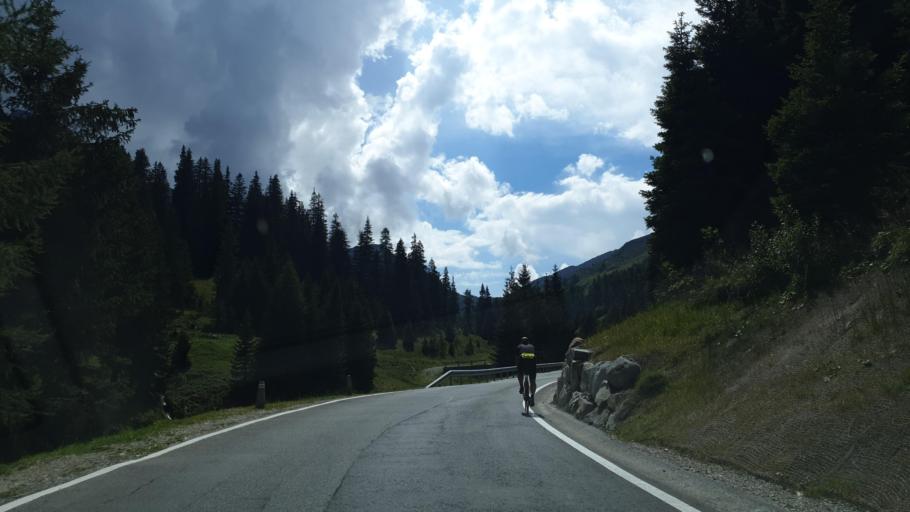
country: CH
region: Grisons
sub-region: Hinterrhein District
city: Hinterrhein
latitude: 46.5361
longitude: 9.3264
